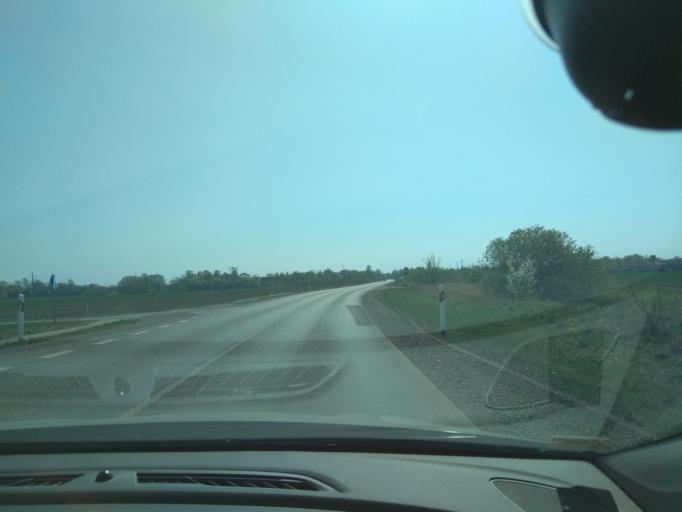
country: LT
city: Linkuva
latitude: 56.0326
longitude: 23.9487
